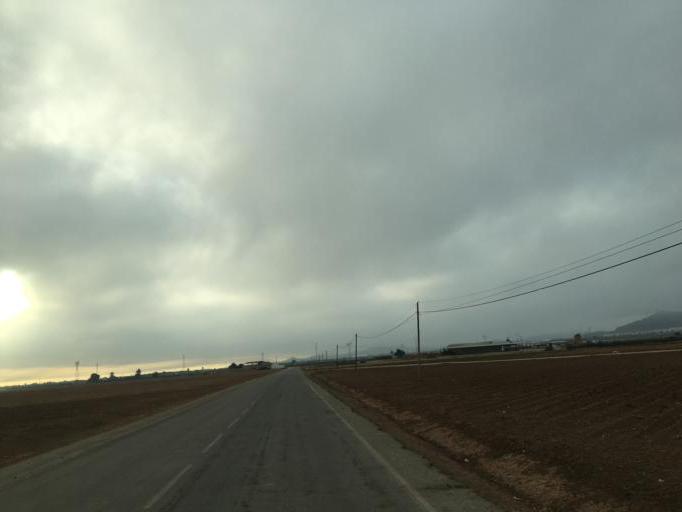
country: ES
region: Murcia
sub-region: Murcia
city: Cartagena
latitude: 37.6641
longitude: -0.9502
